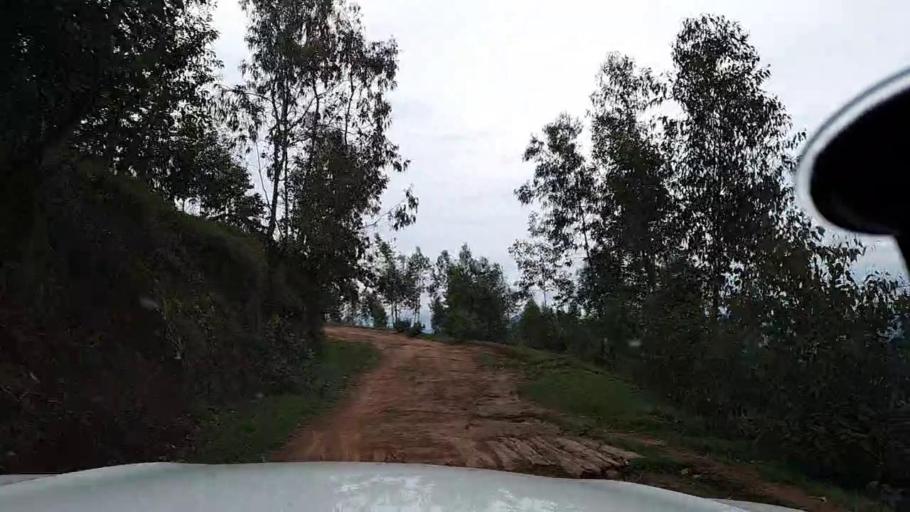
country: RW
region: Southern Province
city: Gitarama
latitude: -2.1233
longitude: 29.6493
